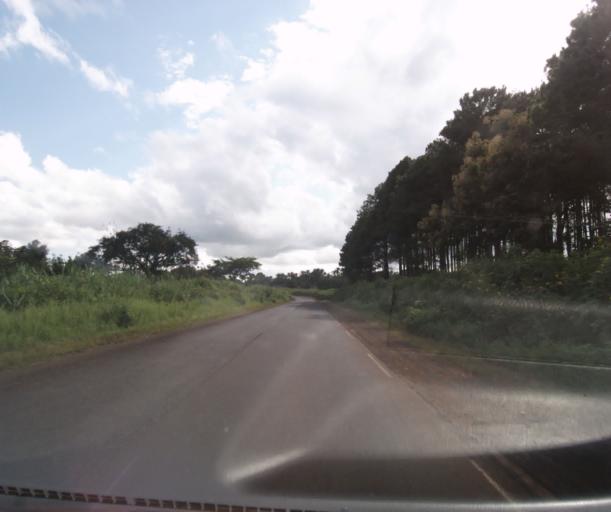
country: CM
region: West
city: Foumban
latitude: 5.6978
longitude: 10.8141
